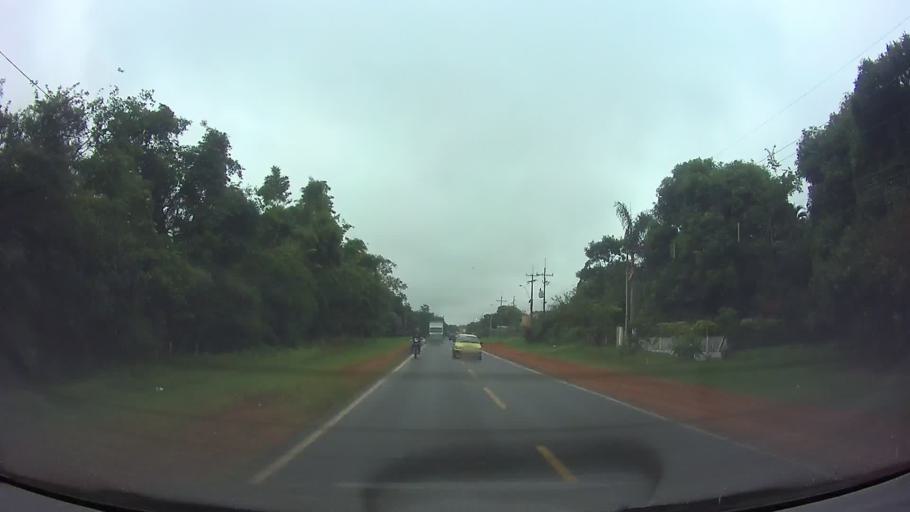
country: PY
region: Central
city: Itaugua
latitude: -25.4150
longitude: -57.3614
